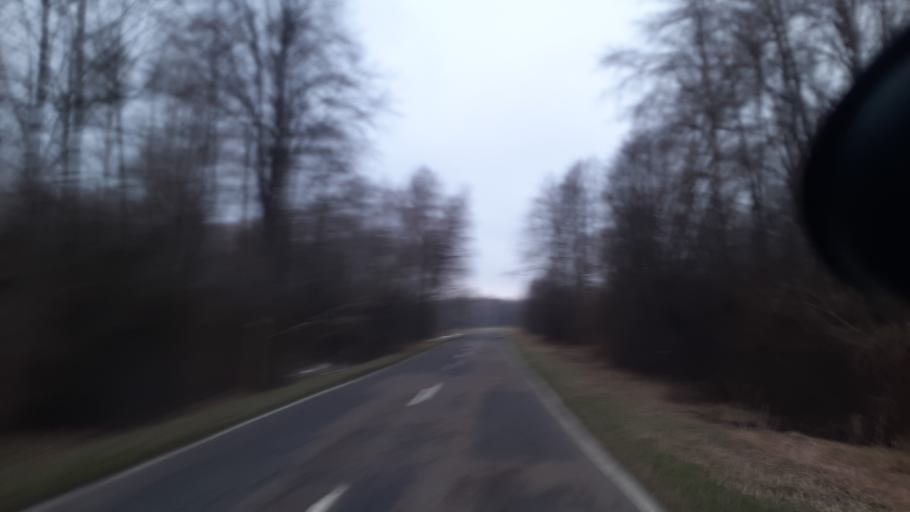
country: PL
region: Lublin Voivodeship
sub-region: Powiat parczewski
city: Sosnowica
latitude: 51.6010
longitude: 23.1389
